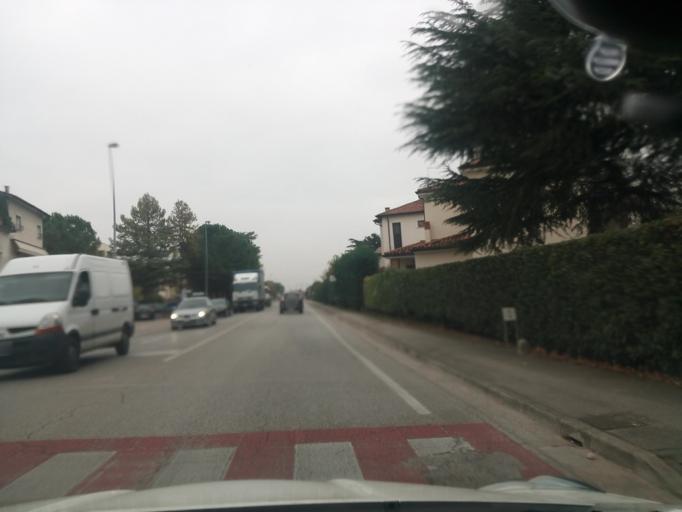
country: IT
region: Veneto
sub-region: Provincia di Vicenza
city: Sandrigo
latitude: 45.6635
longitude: 11.5986
